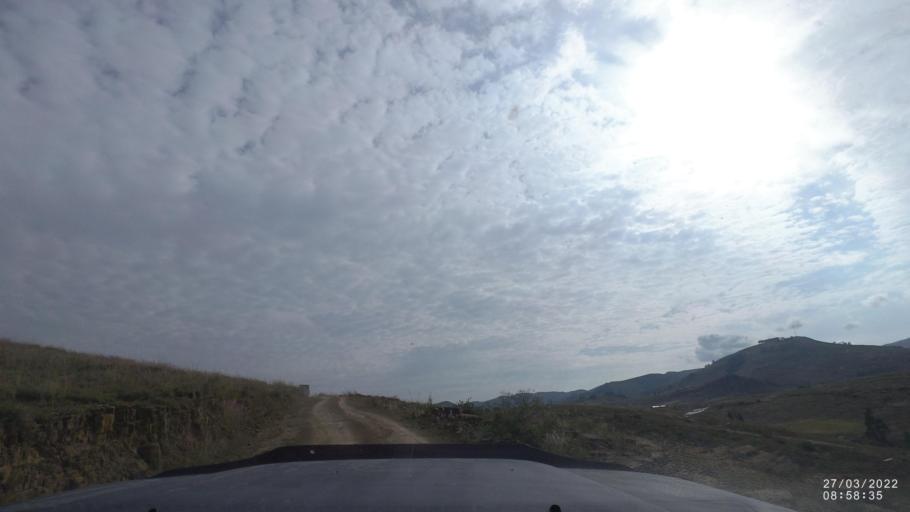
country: BO
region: Cochabamba
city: Cliza
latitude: -17.7422
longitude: -65.8565
